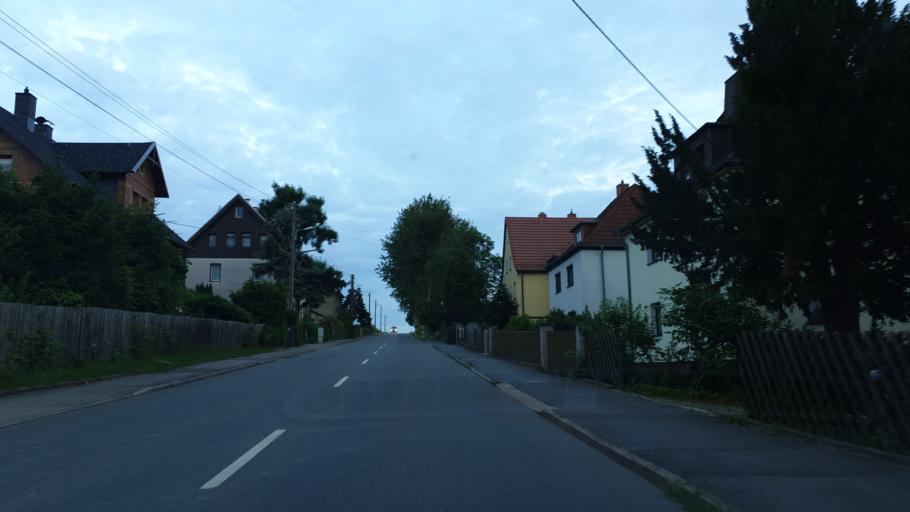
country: DE
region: Saxony
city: Hohenstein-Ernstthal
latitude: 50.7964
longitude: 12.7163
